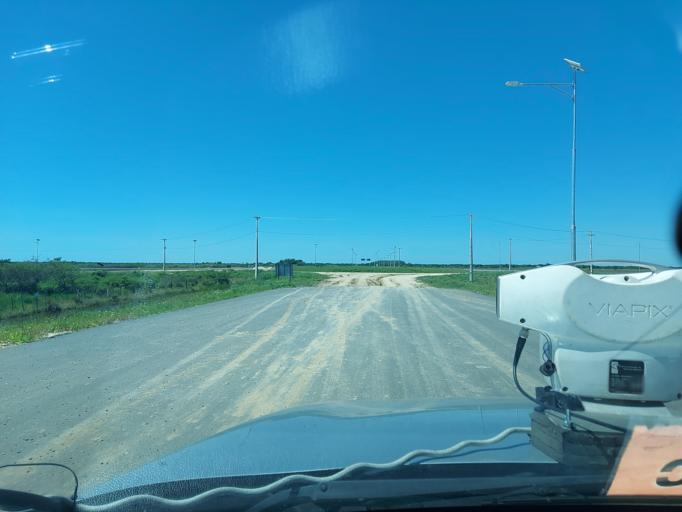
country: PY
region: Neembucu
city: Pilar
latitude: -26.8481
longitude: -58.2312
